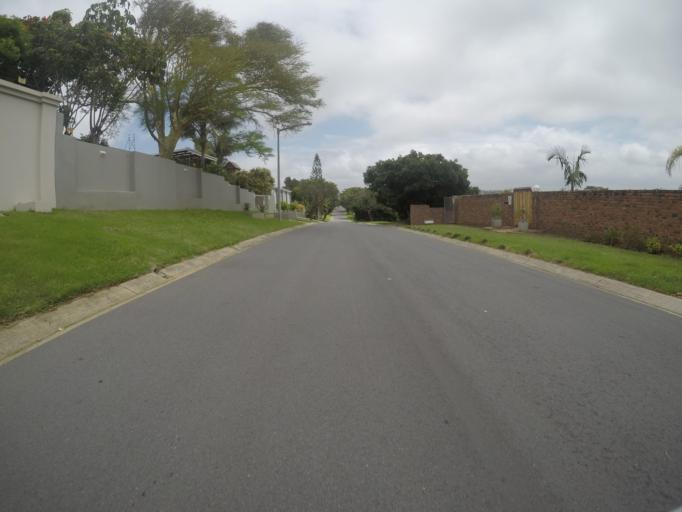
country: ZA
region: Eastern Cape
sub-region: Buffalo City Metropolitan Municipality
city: East London
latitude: -32.9924
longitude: 27.9329
